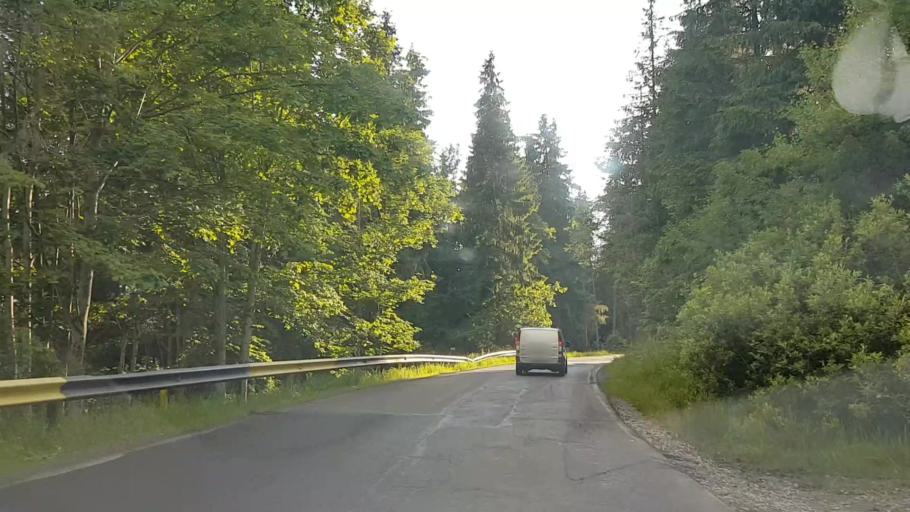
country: RO
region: Harghita
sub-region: Comuna Varsag
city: Varsag
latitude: 46.6628
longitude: 25.3178
